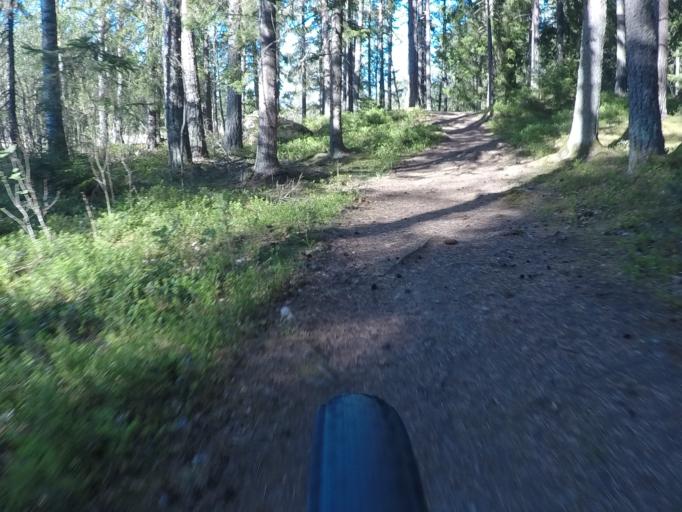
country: SE
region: Soedermanland
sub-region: Eskilstuna Kommun
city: Eskilstuna
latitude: 59.4002
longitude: 16.5436
